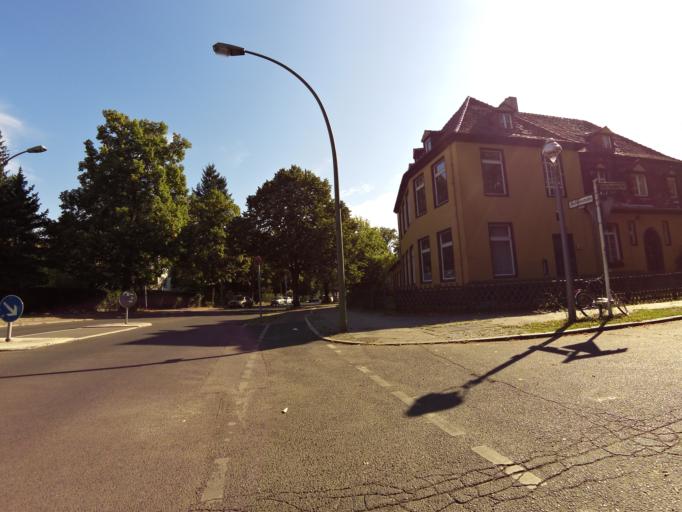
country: DE
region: Berlin
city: Zehlendorf Bezirk
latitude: 52.4303
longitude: 13.2630
